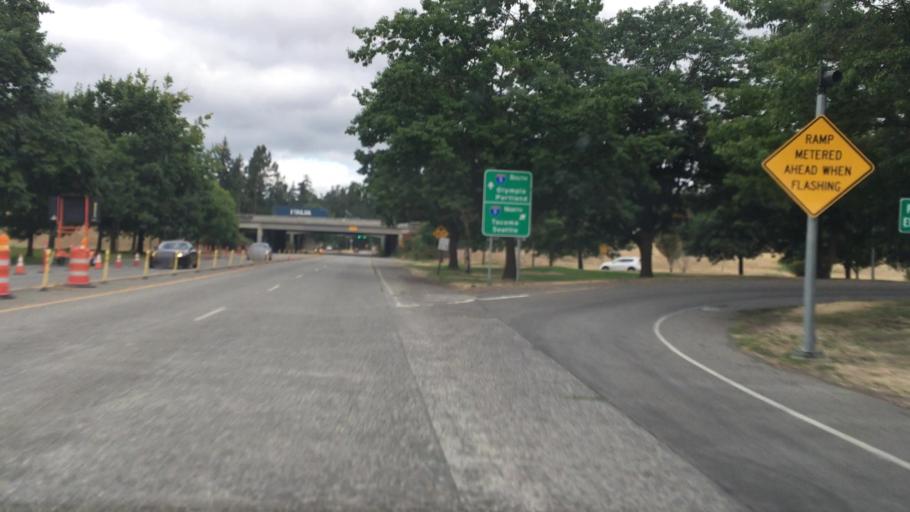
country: US
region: Washington
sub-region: Pierce County
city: Fort Lewis
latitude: 47.1025
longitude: -122.5872
